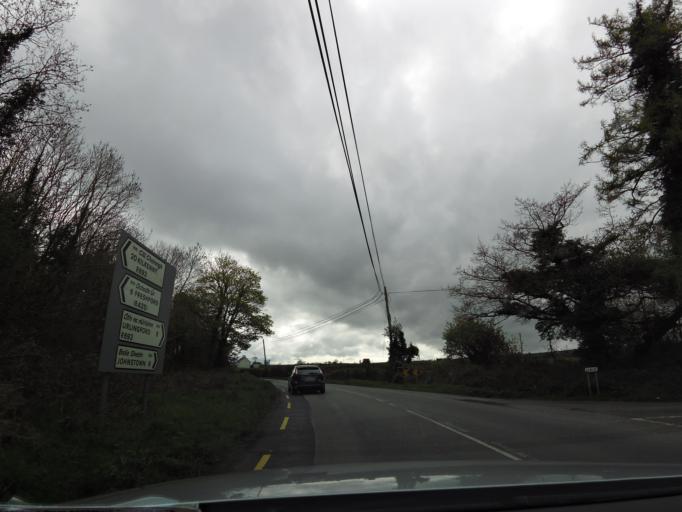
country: IE
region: Leinster
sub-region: Kilkenny
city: Ballyragget
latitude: 52.7315
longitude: -7.4523
